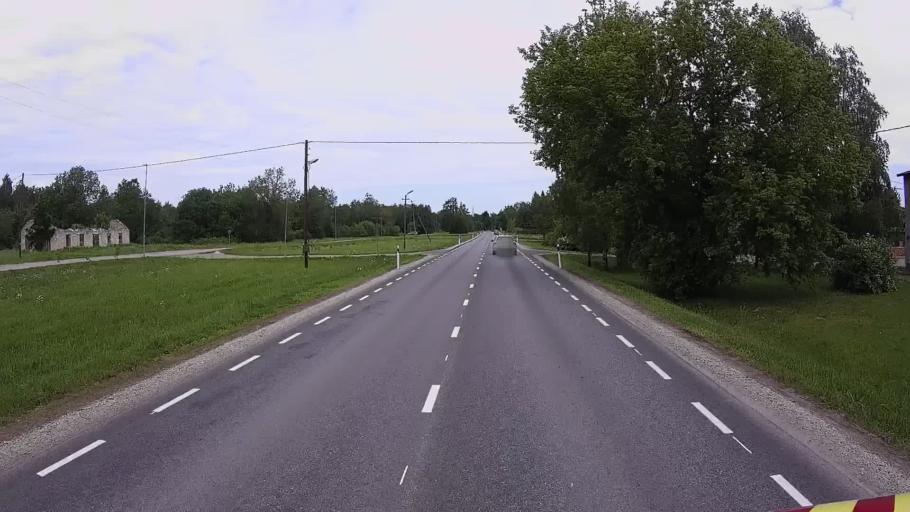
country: EE
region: Laeaene-Virumaa
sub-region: Vaeike-Maarja vald
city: Vaike-Maarja
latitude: 59.1192
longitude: 26.2473
